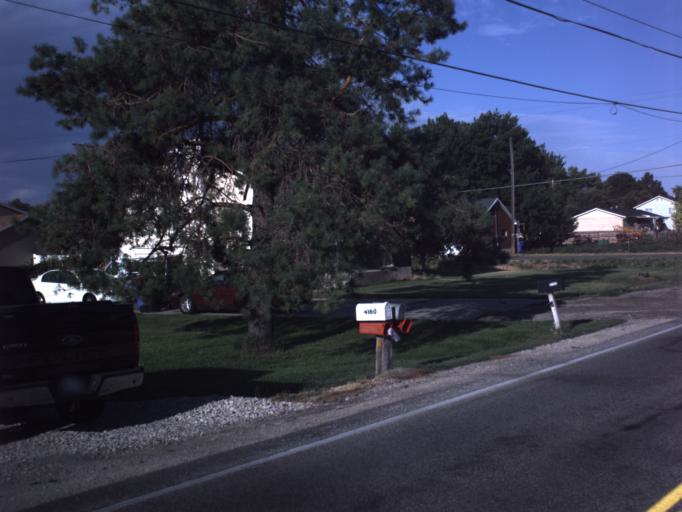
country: US
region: Utah
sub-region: Weber County
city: Plain City
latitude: 41.3054
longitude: -112.0801
